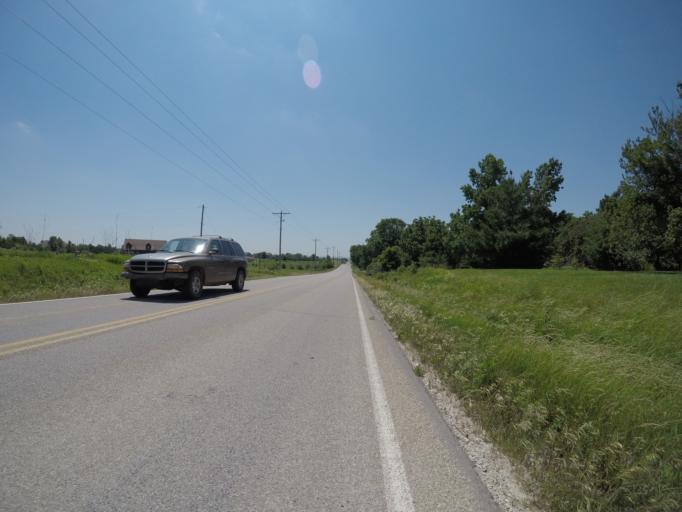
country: US
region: Kansas
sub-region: Riley County
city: Manhattan
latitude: 39.2143
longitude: -96.4406
